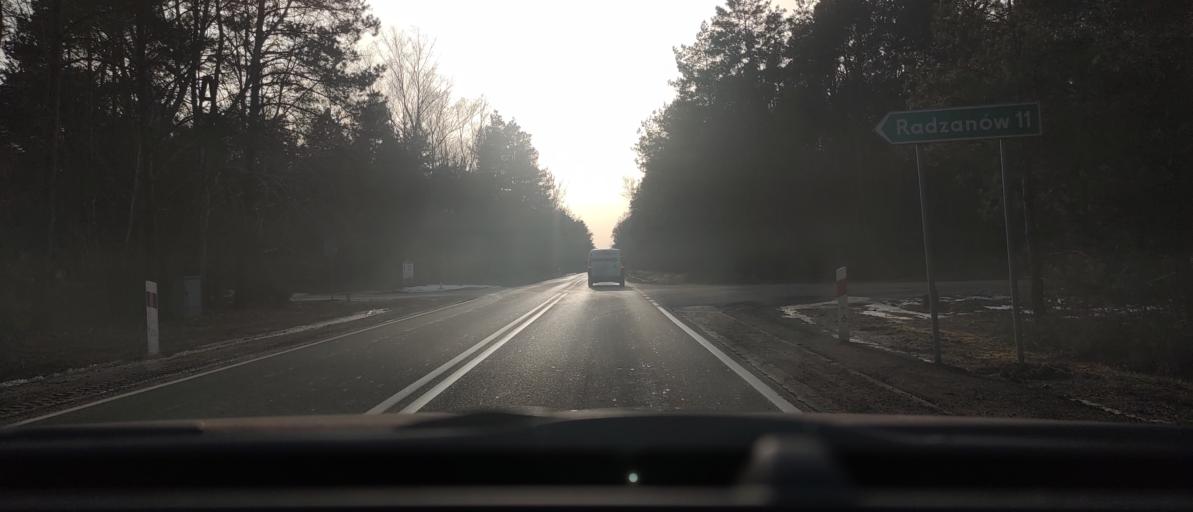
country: PL
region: Masovian Voivodeship
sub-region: Powiat bialobrzeski
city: Bialobrzegi
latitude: 51.6411
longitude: 20.9160
